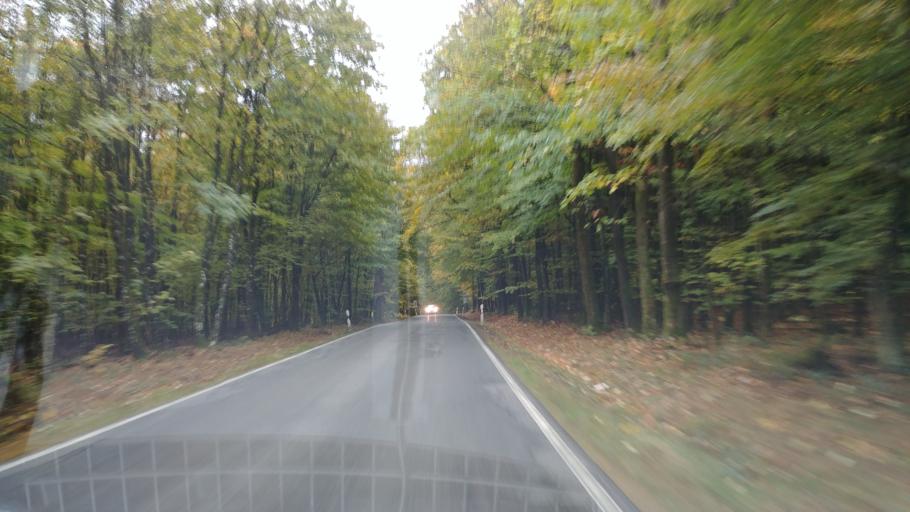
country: DE
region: Hesse
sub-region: Regierungsbezirk Darmstadt
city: Walluf
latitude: 50.0799
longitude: 8.1364
